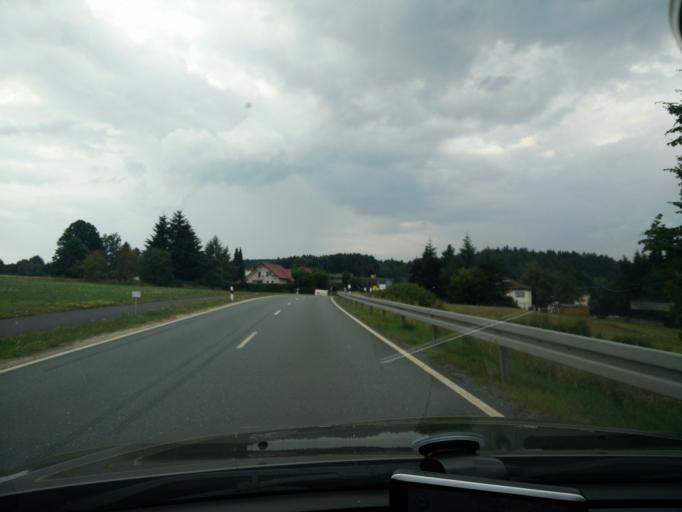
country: DE
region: Bavaria
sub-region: Upper Franconia
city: Fichtelberg
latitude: 49.9951
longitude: 11.8512
